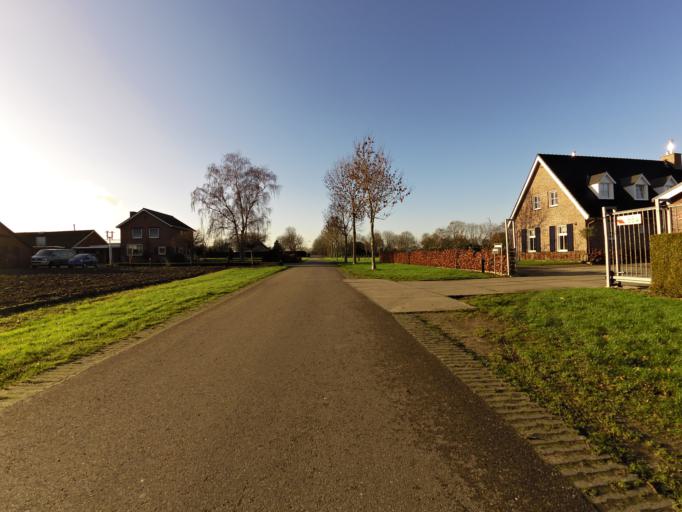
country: NL
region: Gelderland
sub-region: Gemeente Zevenaar
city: Zevenaar
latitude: 51.9334
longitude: 6.1197
